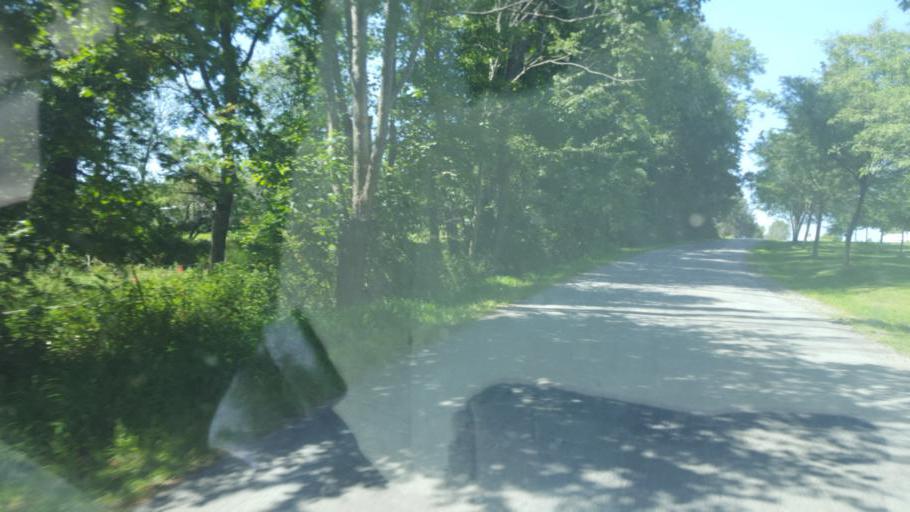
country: US
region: Pennsylvania
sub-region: Clarion County
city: Knox
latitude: 41.1925
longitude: -79.6734
